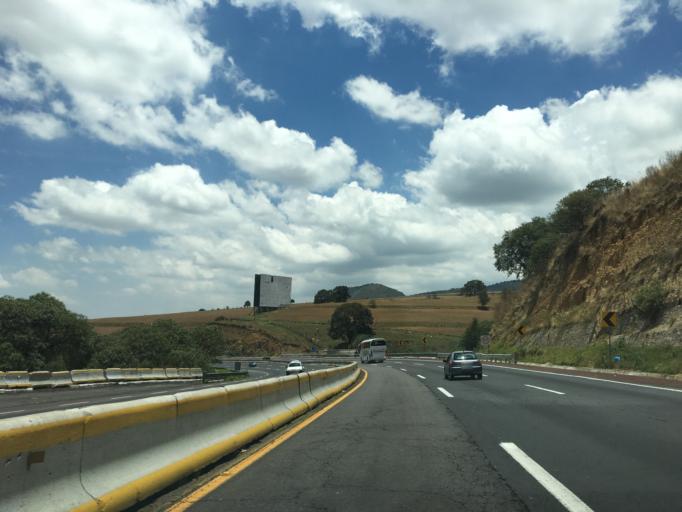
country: MX
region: Mexico
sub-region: Ixtapaluca
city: San Jeronimo Cuatro Vientos
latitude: 19.3008
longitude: -98.7765
